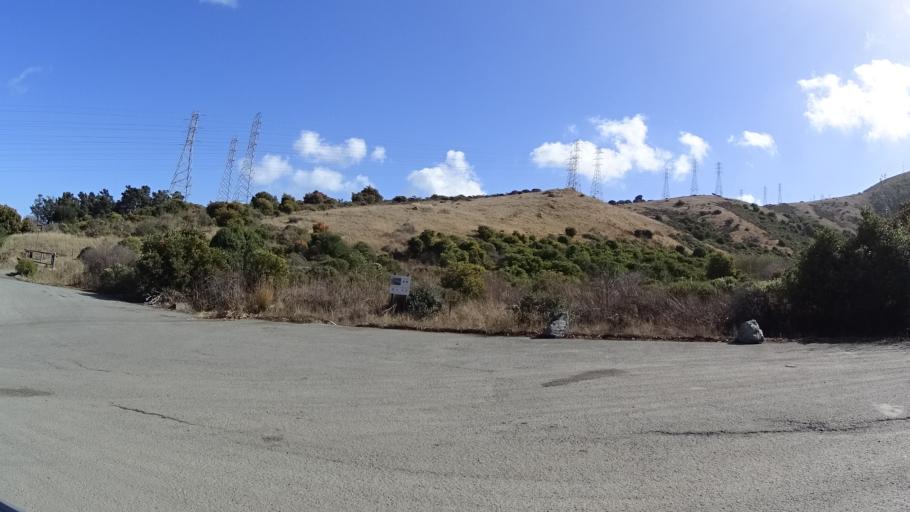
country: US
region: California
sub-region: San Mateo County
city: Brisbane
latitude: 37.6858
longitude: -122.4119
